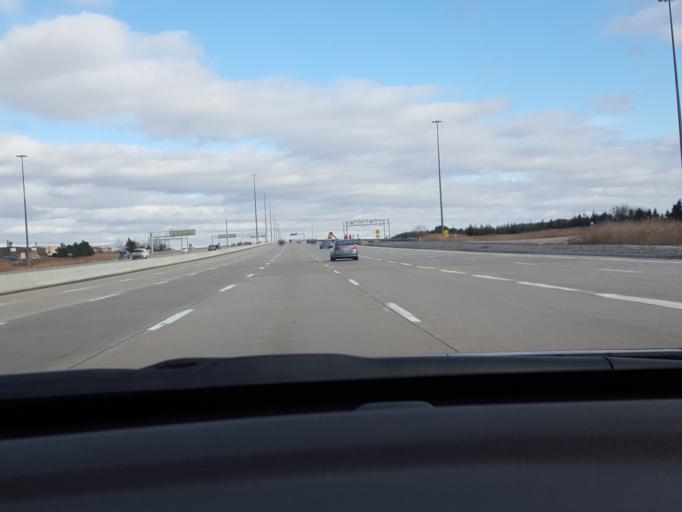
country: CA
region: Ontario
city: Concord
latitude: 43.7863
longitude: -79.5221
